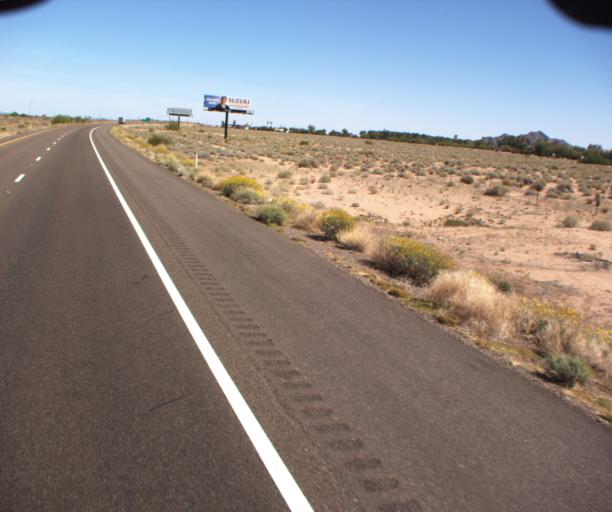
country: US
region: Arizona
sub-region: Yuma County
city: Wellton
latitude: 32.7962
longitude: -113.5494
